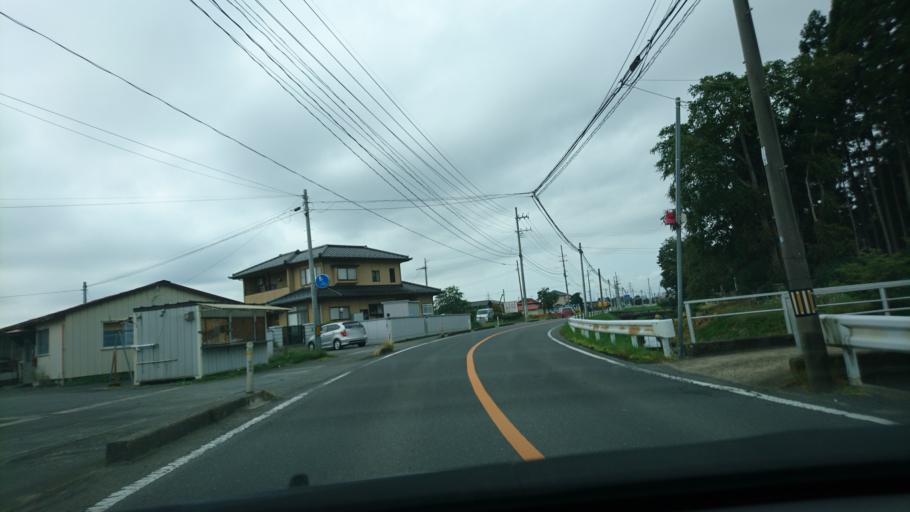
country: JP
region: Miyagi
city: Furukawa
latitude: 38.7437
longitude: 141.0438
